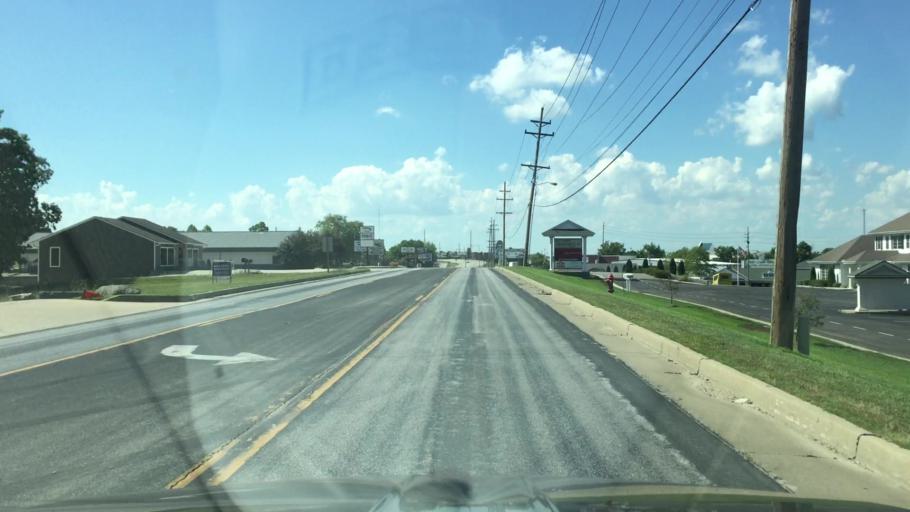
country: US
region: Missouri
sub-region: Camden County
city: Osage Beach
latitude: 38.1514
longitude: -92.6004
